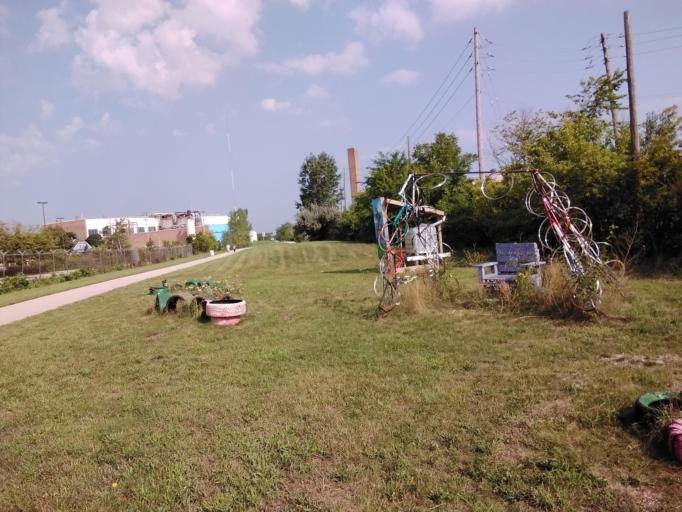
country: US
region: Wisconsin
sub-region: Milwaukee County
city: Shorewood
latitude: 43.0841
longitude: -87.9090
